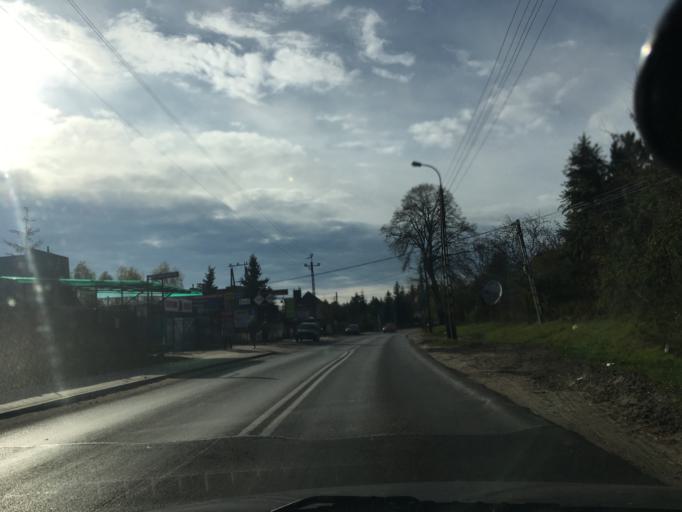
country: PL
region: Masovian Voivodeship
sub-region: Powiat piaseczynski
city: Piaseczno
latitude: 52.0546
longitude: 21.0070
